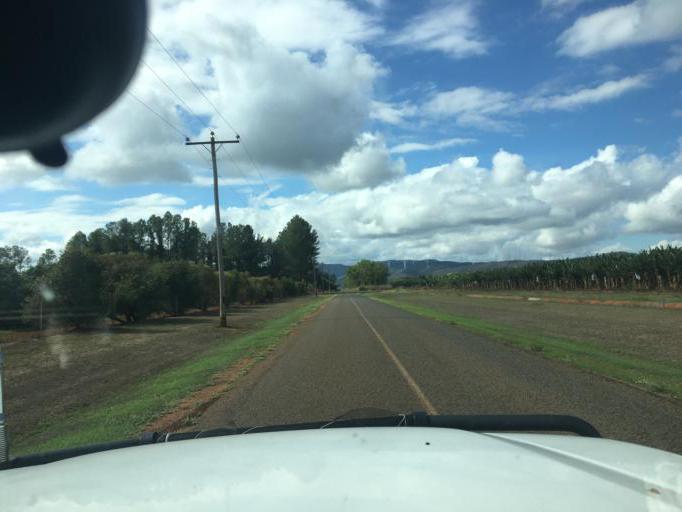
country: AU
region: Queensland
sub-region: Tablelands
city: Mareeba
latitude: -17.1050
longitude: 145.4113
